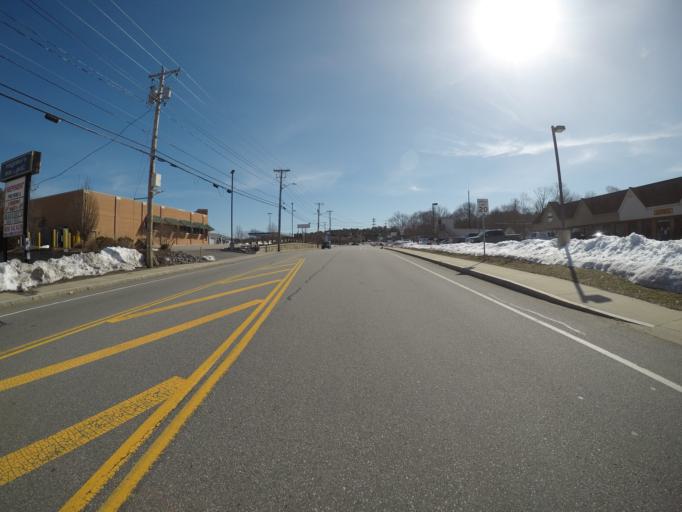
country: US
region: Massachusetts
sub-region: Bristol County
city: Easton
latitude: 42.0236
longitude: -71.1221
